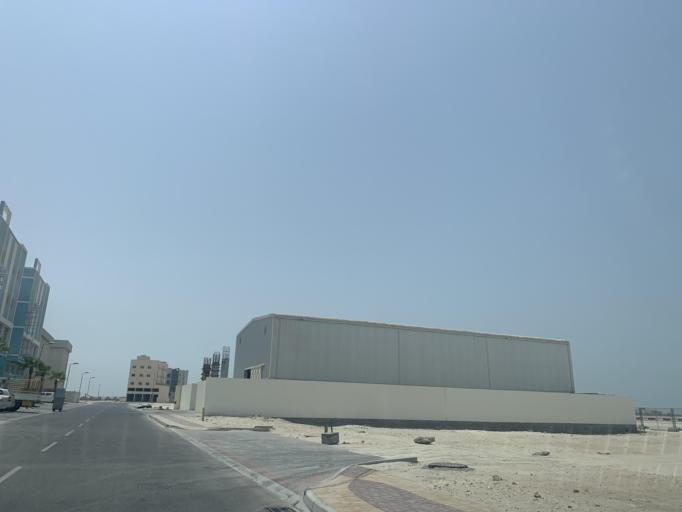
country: BH
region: Muharraq
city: Al Hadd
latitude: 26.2615
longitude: 50.6693
